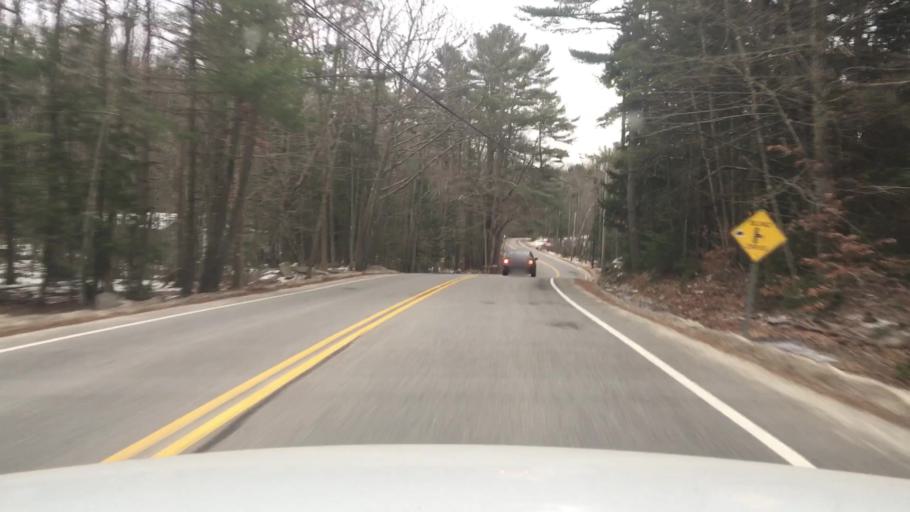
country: US
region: Maine
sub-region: Cumberland County
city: Freeport
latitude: 43.8780
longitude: -70.0474
